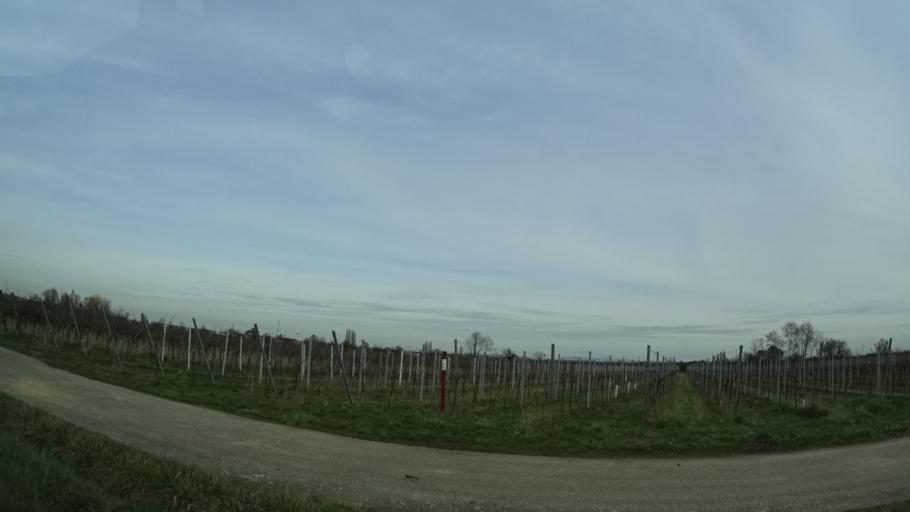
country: DE
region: Rheinland-Pfalz
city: Neustadt
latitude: 49.3327
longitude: 8.1524
